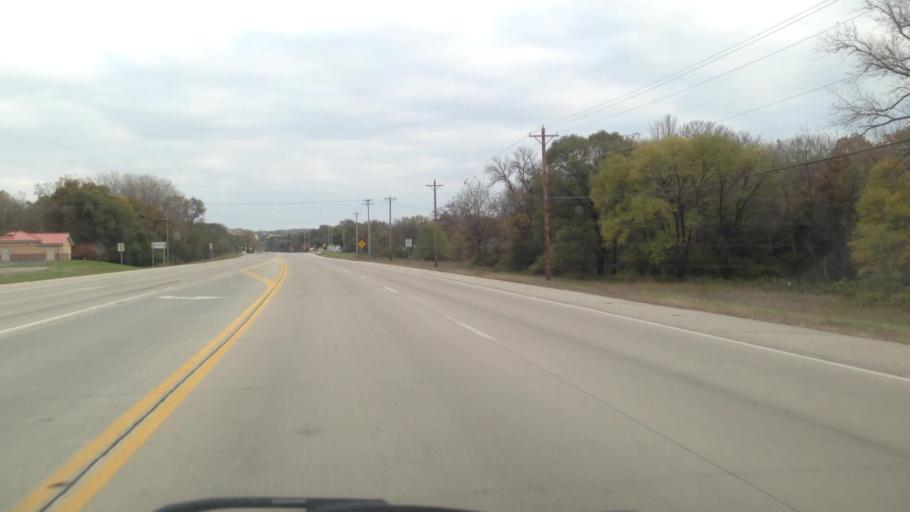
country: US
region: Minnesota
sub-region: Olmsted County
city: Rochester
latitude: 43.9923
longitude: -92.4214
